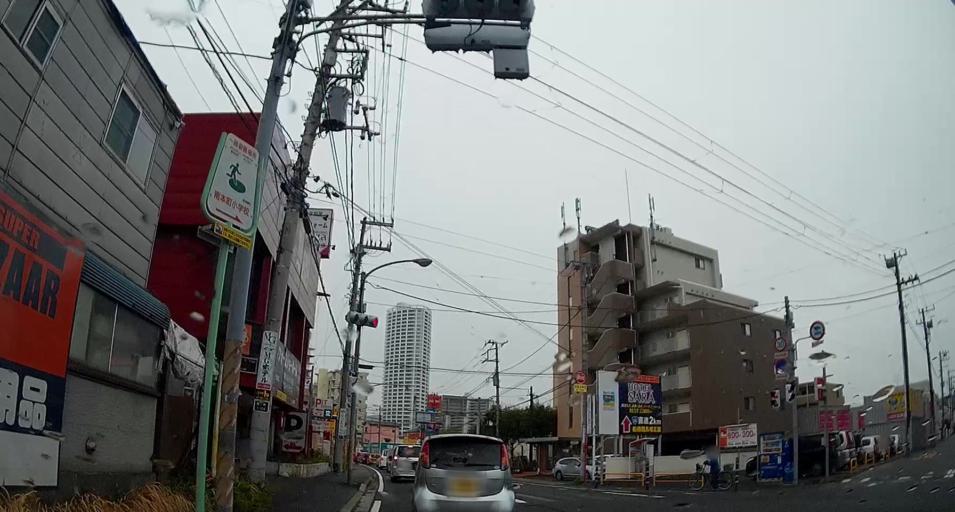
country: JP
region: Chiba
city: Funabashi
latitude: 35.6993
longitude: 139.9772
